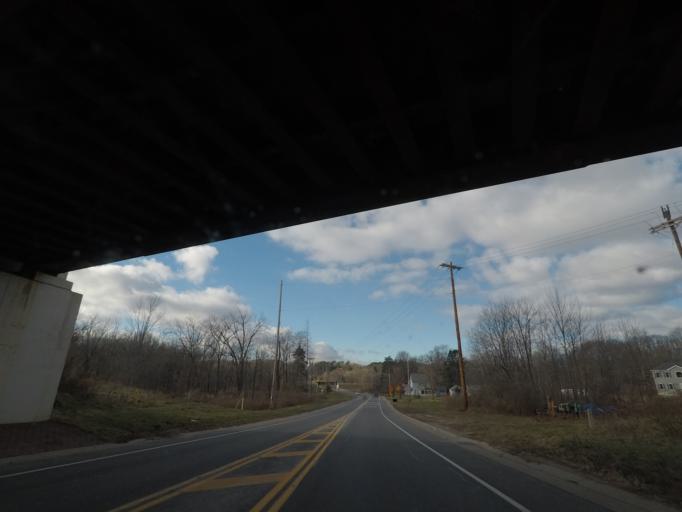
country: US
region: New York
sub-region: Schenectady County
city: East Glenville
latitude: 42.8668
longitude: -73.8984
